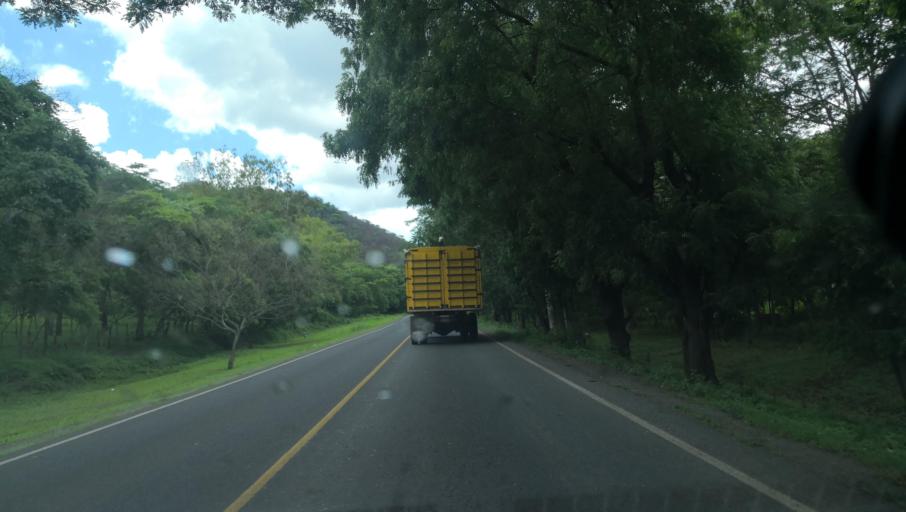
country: NI
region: Madriz
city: Yalaguina
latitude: 13.4589
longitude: -86.4641
